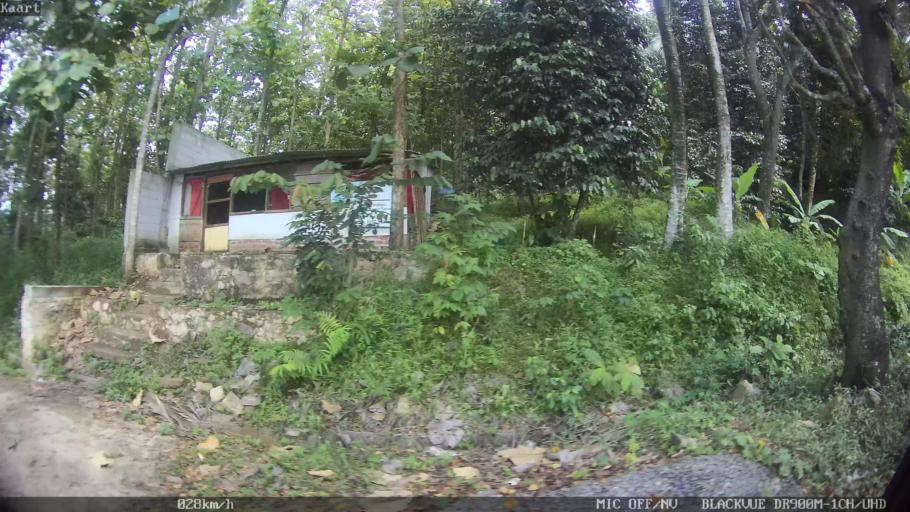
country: ID
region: Lampung
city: Bandarlampung
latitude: -5.4605
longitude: 105.2436
